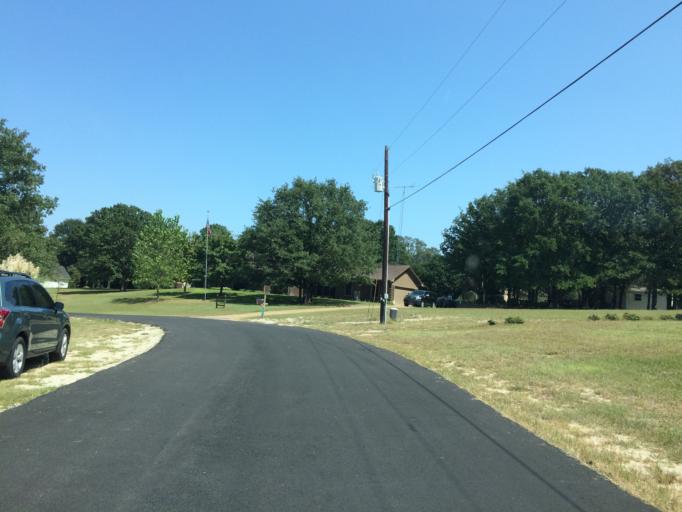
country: US
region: Texas
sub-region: Wood County
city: Hawkins
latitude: 32.7183
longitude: -95.1770
